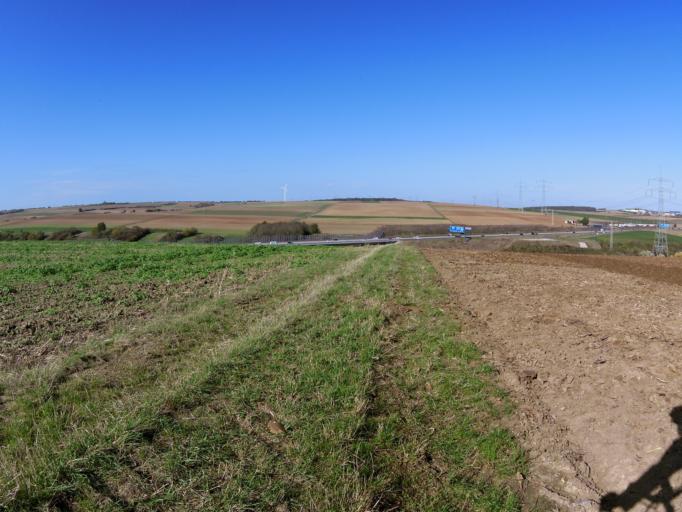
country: DE
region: Bavaria
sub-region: Regierungsbezirk Unterfranken
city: Theilheim
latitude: 49.7529
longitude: 10.0520
